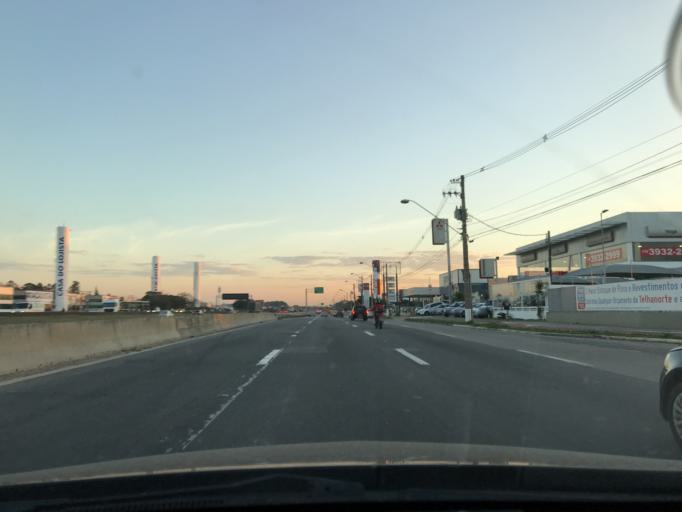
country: BR
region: Sao Paulo
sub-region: Sao Jose Dos Campos
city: Sao Jose dos Campos
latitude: -23.2271
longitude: -45.9084
